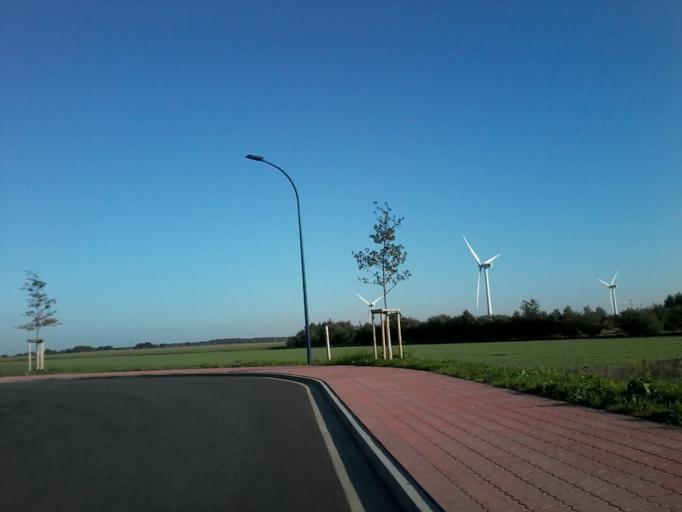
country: DE
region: Lower Saxony
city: Oyten
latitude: 53.0510
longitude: 9.0439
